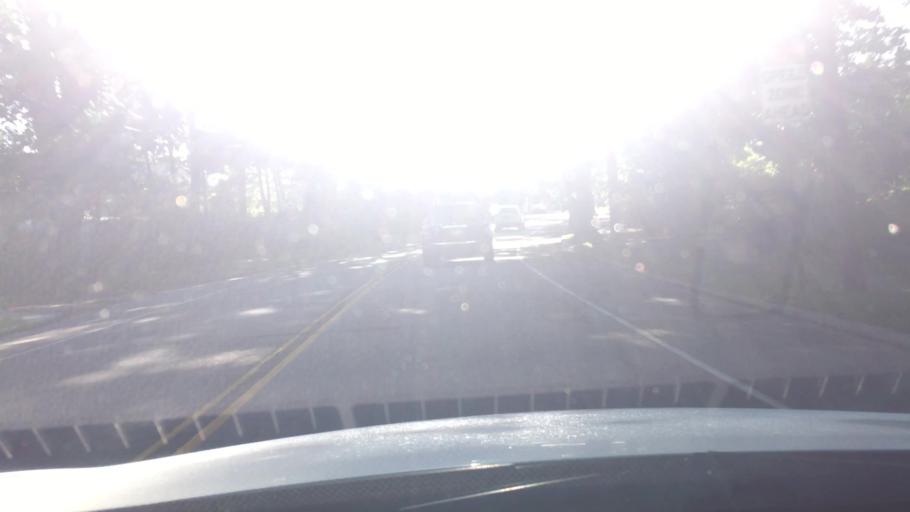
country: US
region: New York
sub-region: Nassau County
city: Albertson
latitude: 40.7723
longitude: -73.6311
